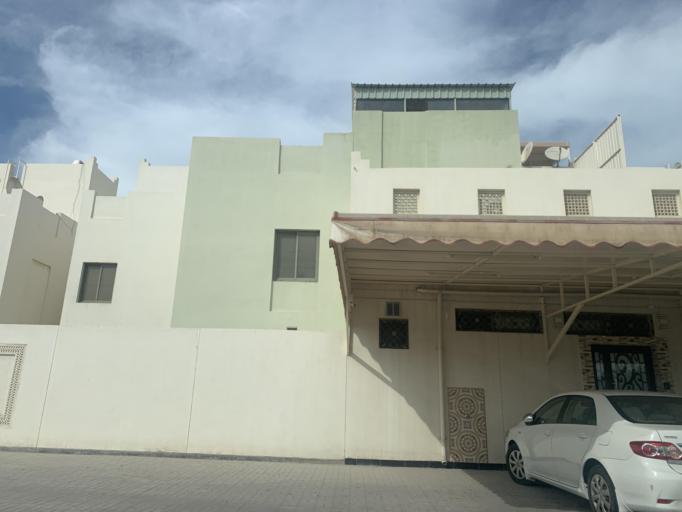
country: BH
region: Central Governorate
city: Madinat Hamad
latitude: 26.1216
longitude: 50.4752
